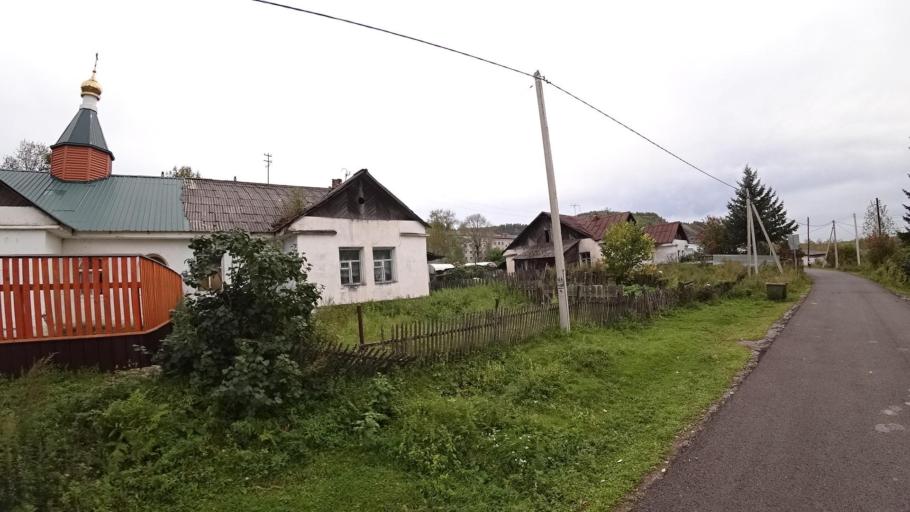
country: RU
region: Jewish Autonomous Oblast
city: Khingansk
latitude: 49.1275
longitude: 131.1920
